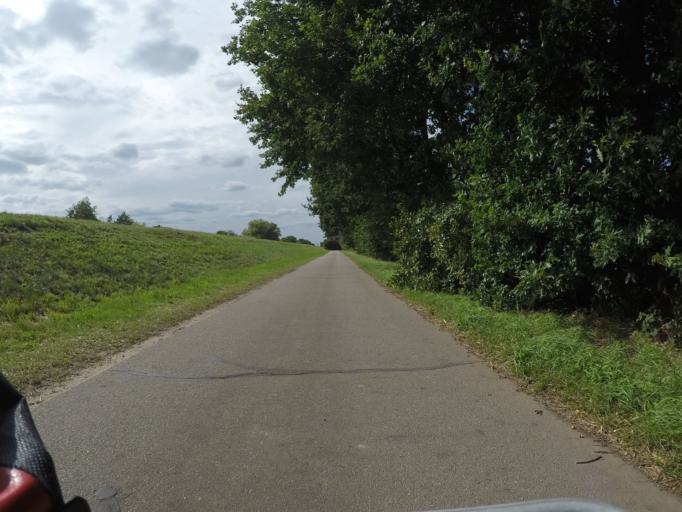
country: DE
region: Lower Saxony
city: Wittorf
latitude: 53.3504
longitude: 10.3774
